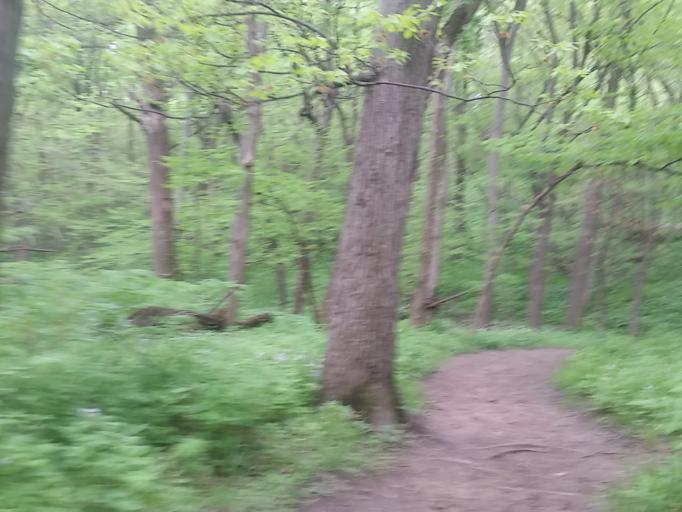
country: US
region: Nebraska
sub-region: Sarpy County
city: Bellevue
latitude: 41.1796
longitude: -95.9172
